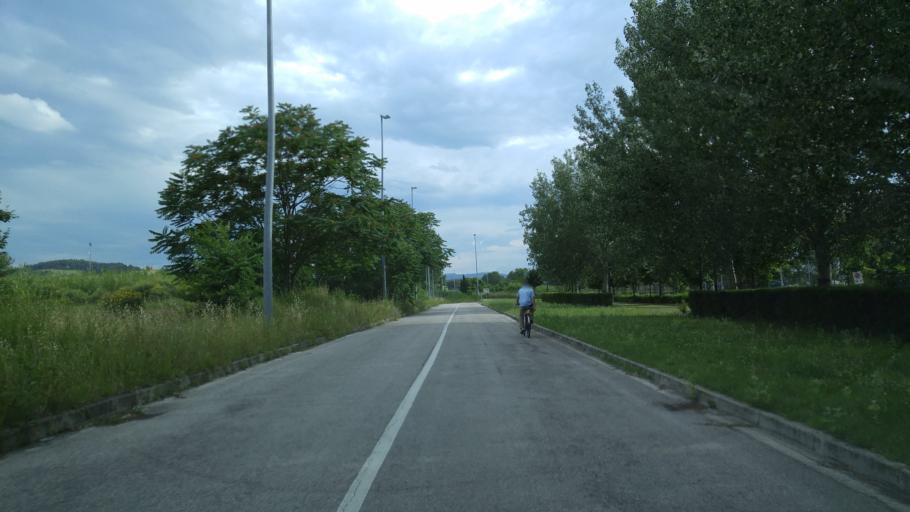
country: IT
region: The Marches
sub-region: Provincia di Pesaro e Urbino
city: Pesaro
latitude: 43.9031
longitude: 12.8688
